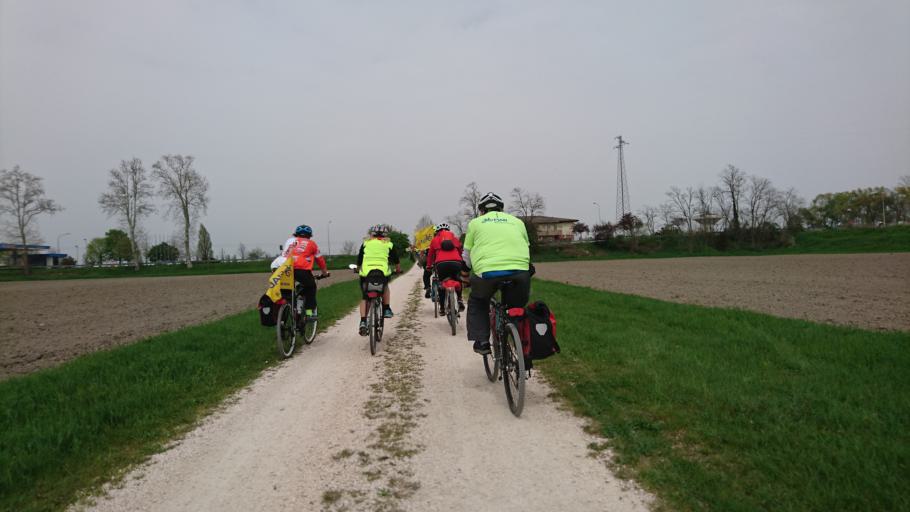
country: IT
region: Veneto
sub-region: Provincia di Venezia
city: Concordia Sagittaria
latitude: 45.7031
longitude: 12.8664
